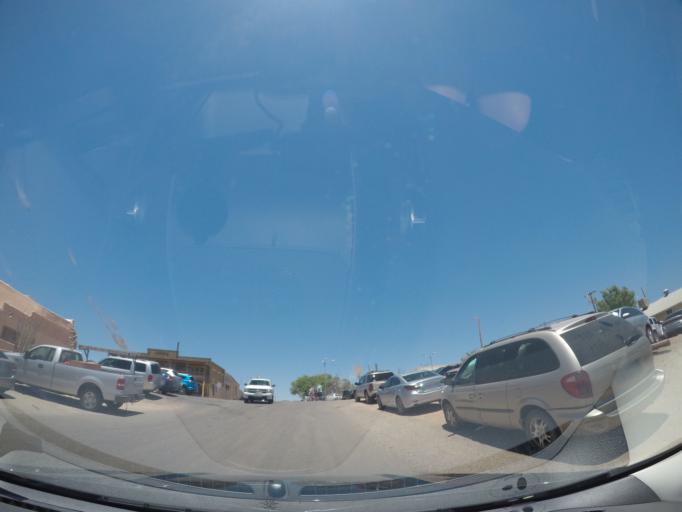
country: US
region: Arizona
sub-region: Cochise County
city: Tombstone
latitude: 31.7116
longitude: -110.0651
